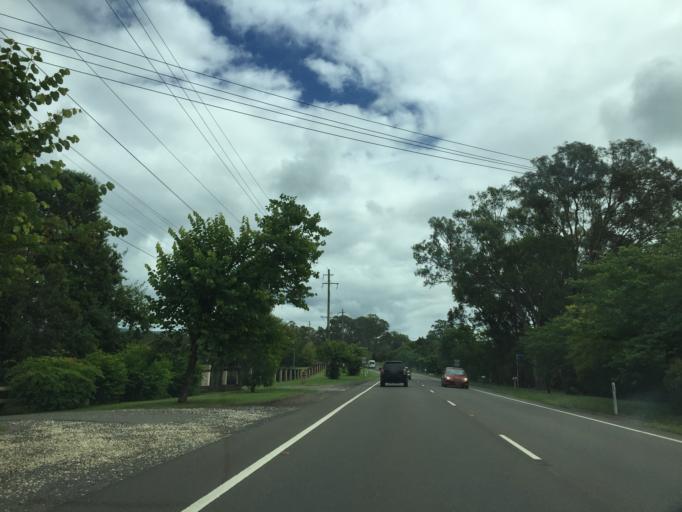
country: AU
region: New South Wales
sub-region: Hawkesbury
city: Richmond
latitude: -33.5601
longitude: 150.7020
